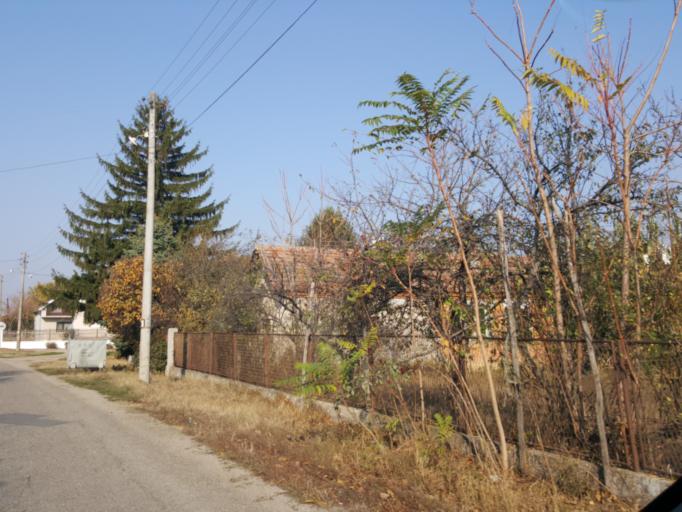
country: RS
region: Central Serbia
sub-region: Borski Okrug
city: Negotin
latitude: 44.2001
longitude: 22.5872
